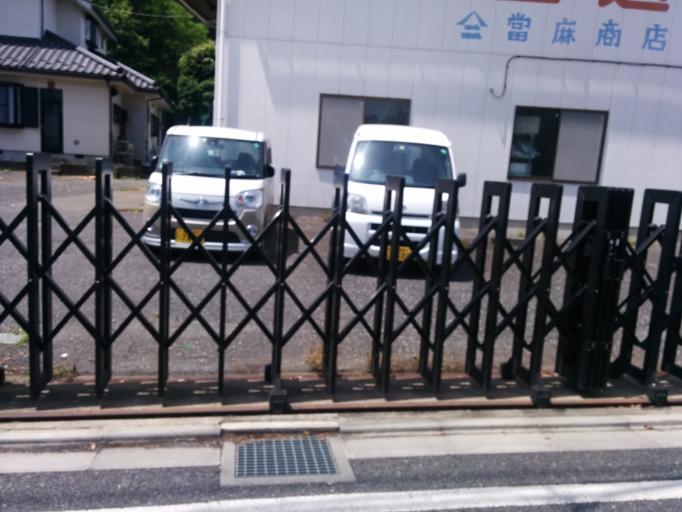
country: JP
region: Tokyo
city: Higashimurayama-shi
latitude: 35.7524
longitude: 139.4834
